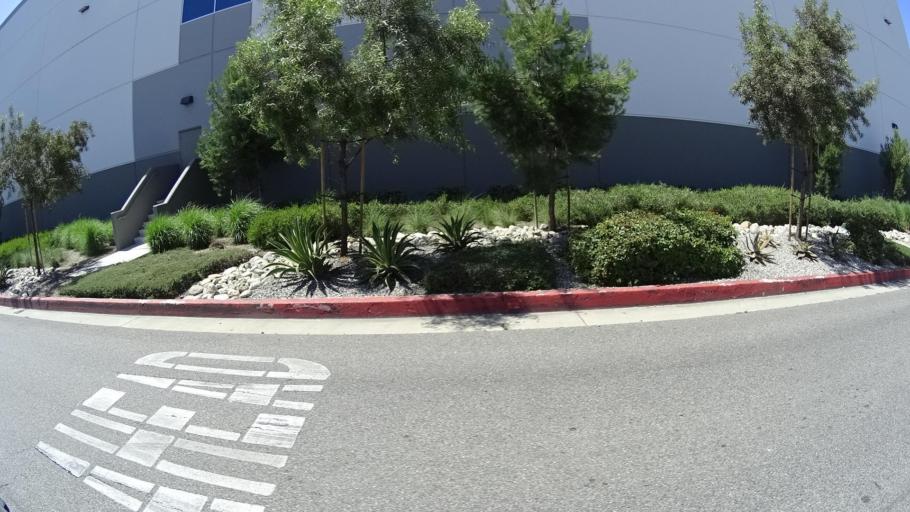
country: US
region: California
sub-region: Los Angeles County
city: La Puente
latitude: 34.0253
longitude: -117.9680
